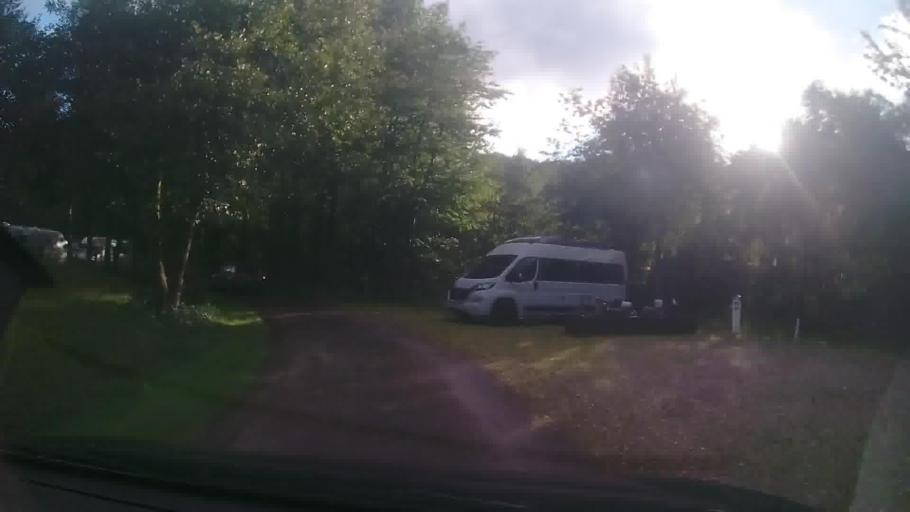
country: GB
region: Scotland
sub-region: Highland
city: Fort William
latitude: 56.6738
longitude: -5.0851
